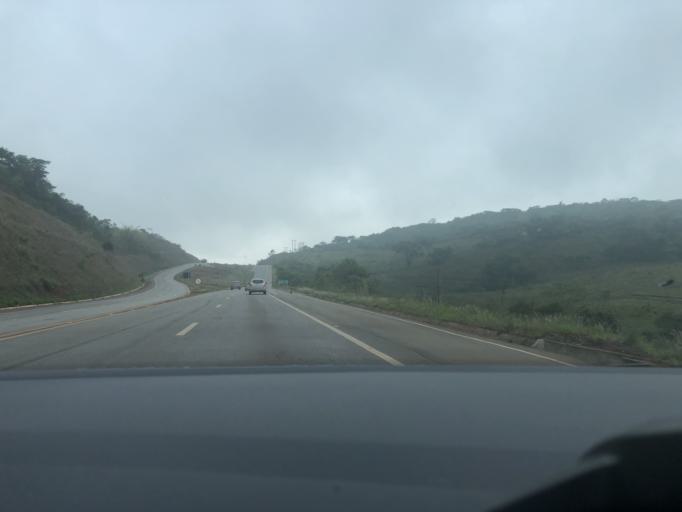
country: BR
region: Minas Gerais
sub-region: Congonhas
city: Congonhas
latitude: -20.5956
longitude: -43.9397
